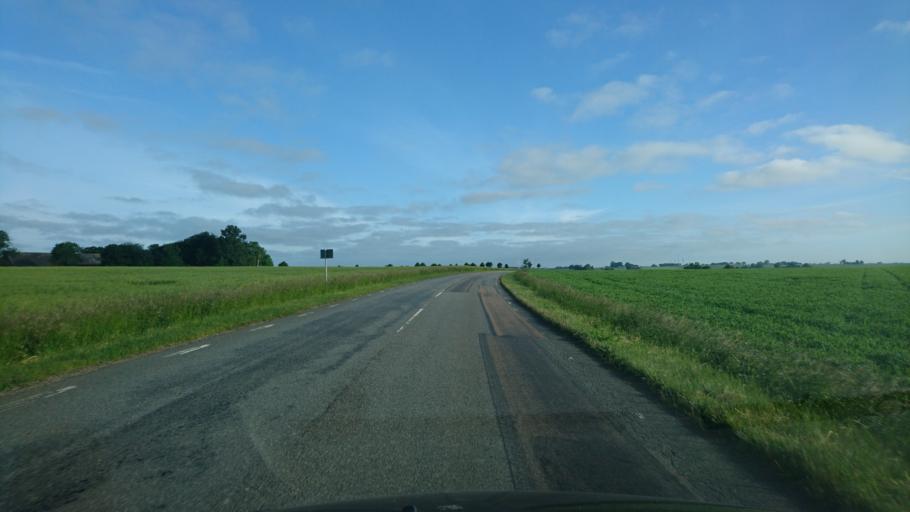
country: SE
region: Skane
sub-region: Tomelilla Kommun
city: Tomelilla
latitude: 55.4642
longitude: 14.0988
